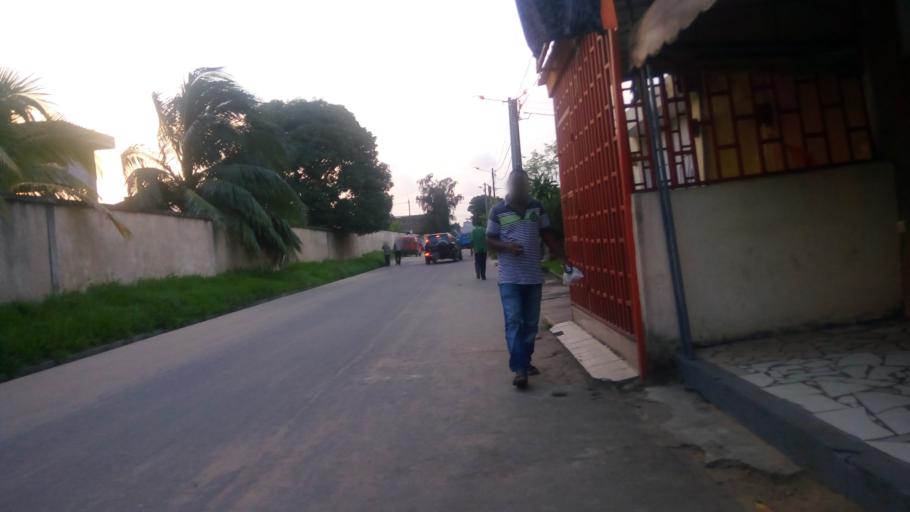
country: CI
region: Lagunes
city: Abobo
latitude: 5.4081
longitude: -3.9909
